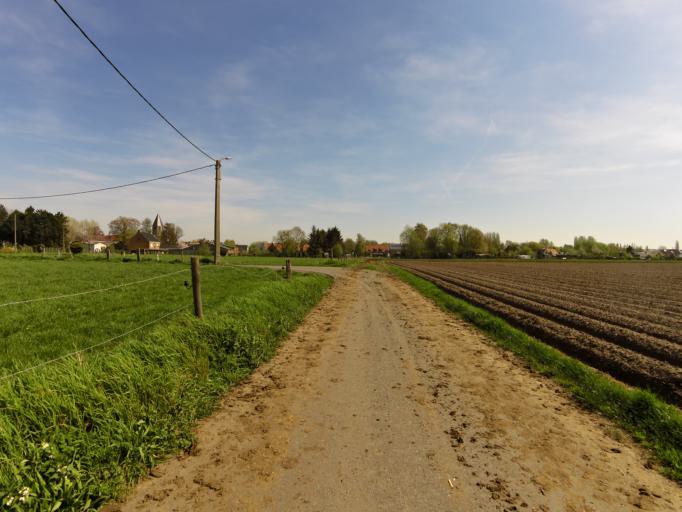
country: BE
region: Flanders
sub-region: Provincie West-Vlaanderen
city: Ichtegem
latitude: 51.0908
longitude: 3.0056
